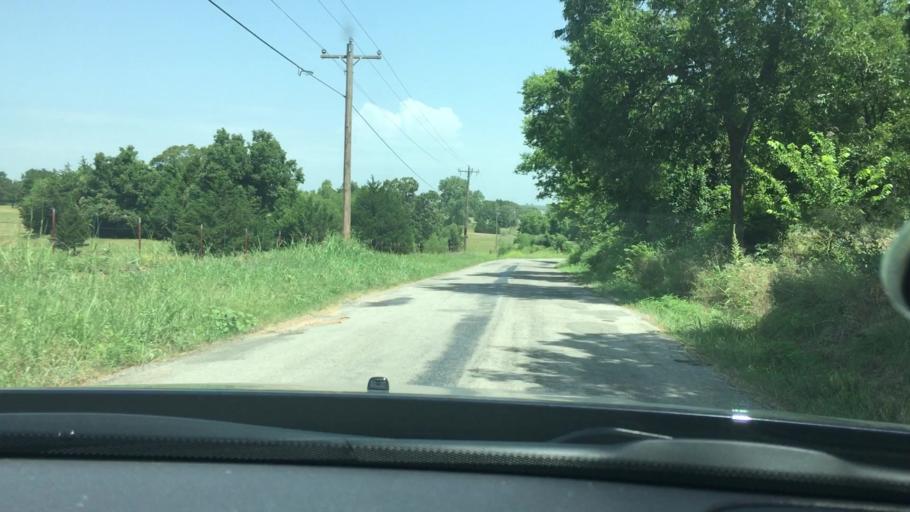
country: US
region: Oklahoma
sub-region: Pontotoc County
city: Byng
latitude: 34.8255
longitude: -96.6699
